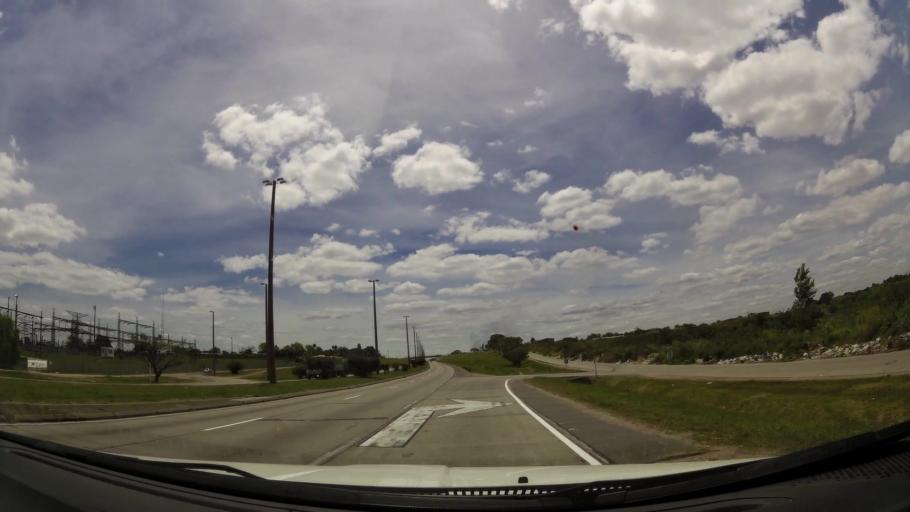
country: UY
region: Montevideo
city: Montevideo
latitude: -34.8499
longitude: -56.2539
